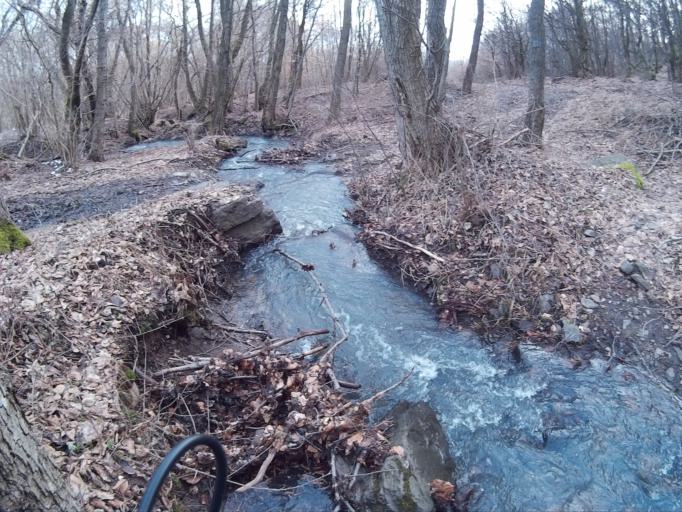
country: HU
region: Borsod-Abauj-Zemplen
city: Gonc
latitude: 48.4016
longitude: 21.3493
